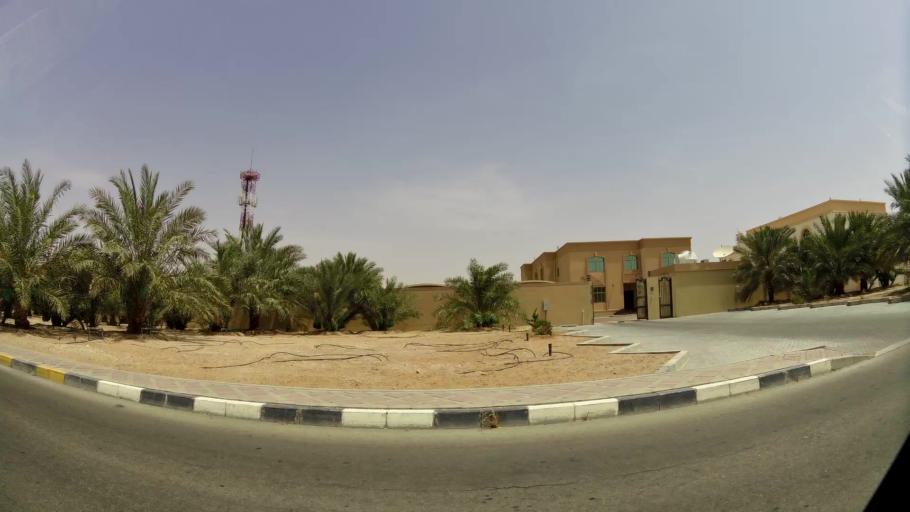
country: AE
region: Abu Dhabi
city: Al Ain
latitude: 24.1994
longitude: 55.7309
